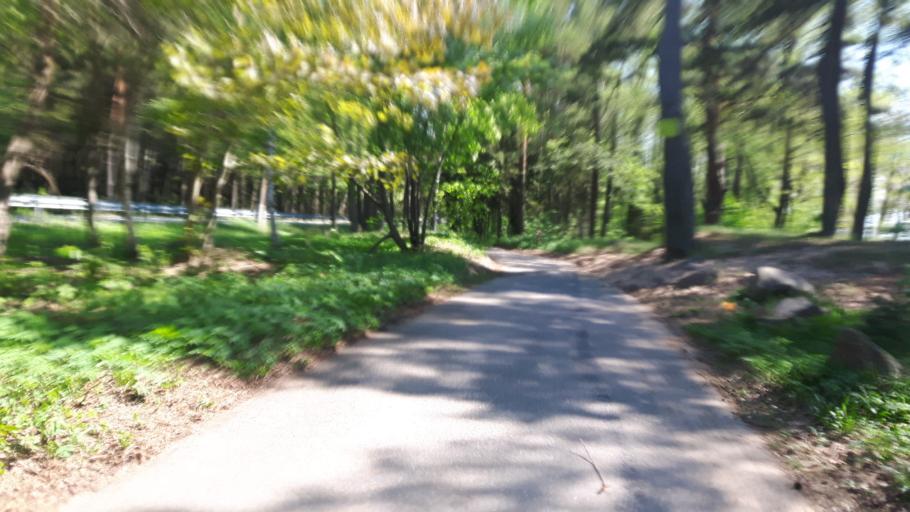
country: RU
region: St.-Petersburg
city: Komarovo
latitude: 60.1782
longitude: 29.7842
